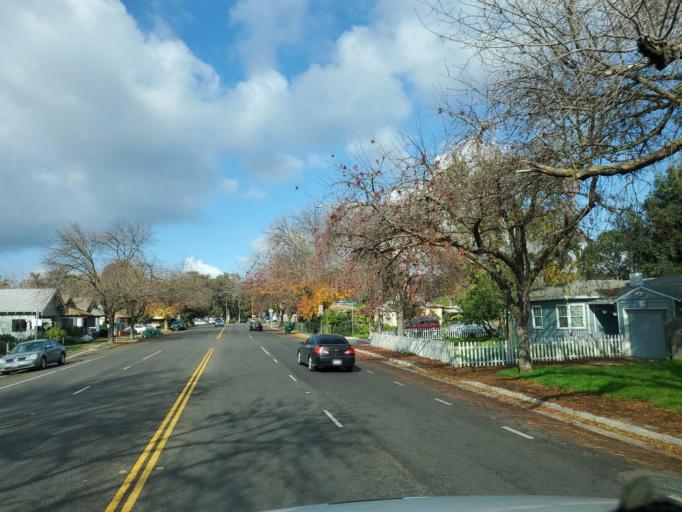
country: US
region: California
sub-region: San Joaquin County
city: Stockton
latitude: 37.9798
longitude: -121.2928
